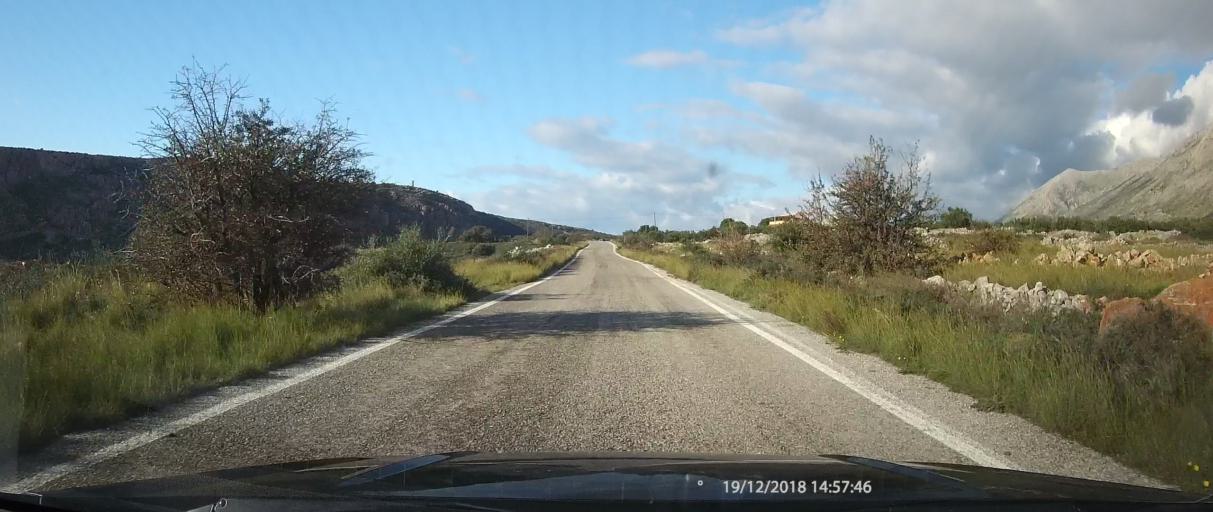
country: GR
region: Peloponnese
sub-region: Nomos Lakonias
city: Gytheio
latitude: 36.4822
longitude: 22.4049
